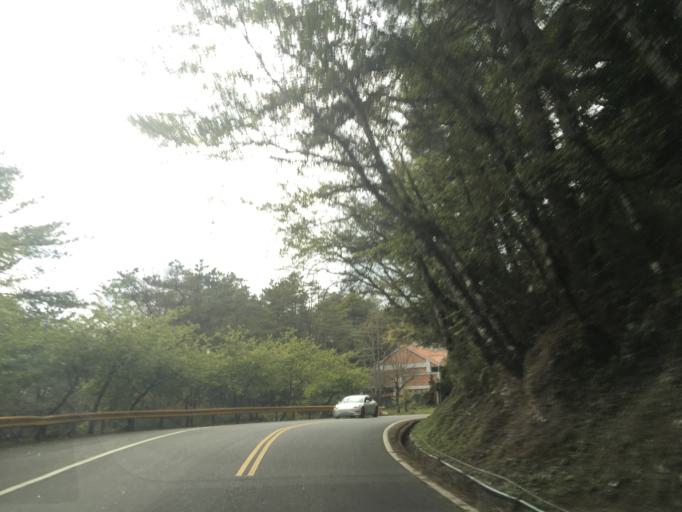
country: TW
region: Taiwan
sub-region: Hualien
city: Hualian
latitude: 24.1864
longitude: 121.3401
